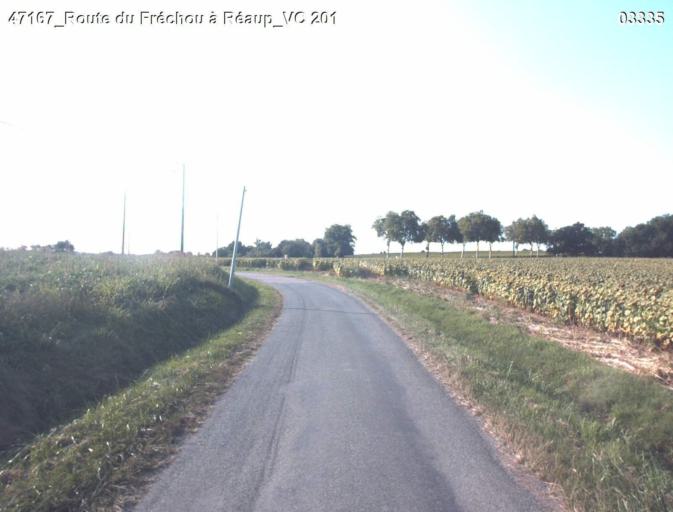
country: FR
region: Aquitaine
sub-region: Departement du Lot-et-Garonne
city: Mezin
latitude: 44.0705
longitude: 0.2759
